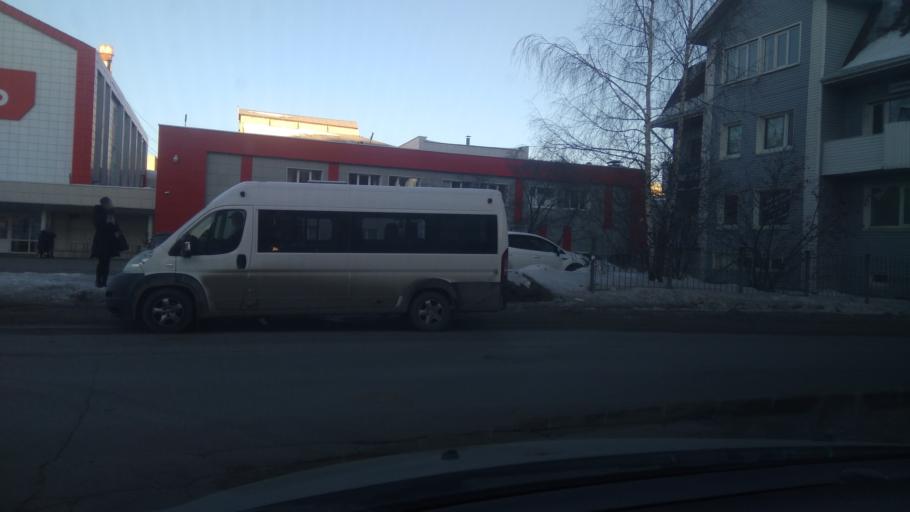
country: RU
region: Sverdlovsk
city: Istok
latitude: 56.8256
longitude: 60.6978
